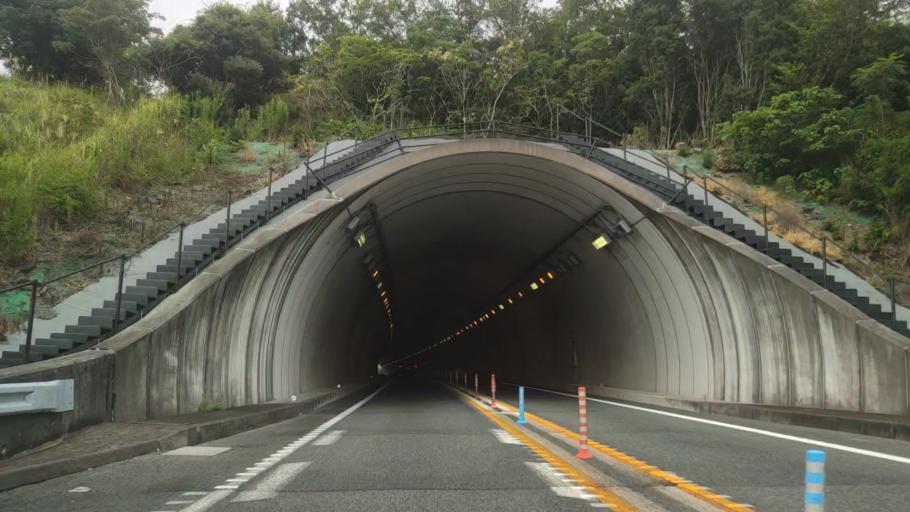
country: JP
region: Wakayama
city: Gobo
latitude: 33.8760
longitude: 135.1871
